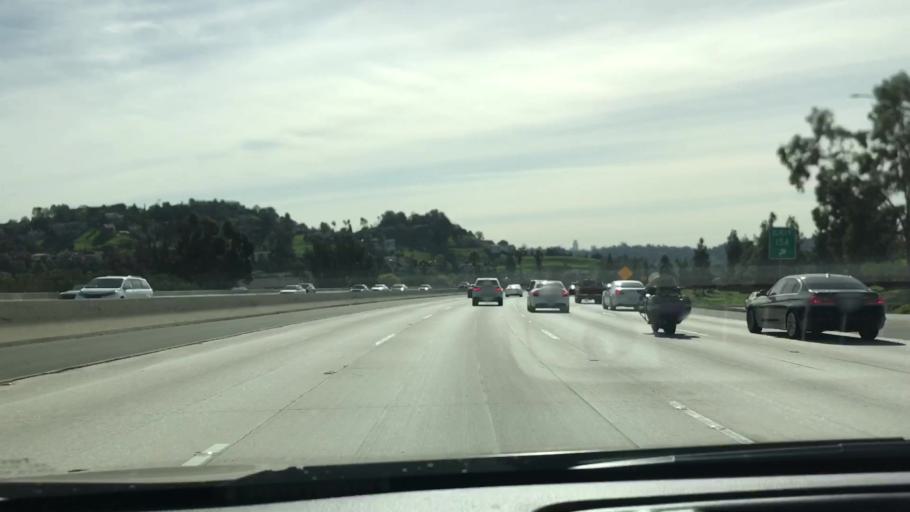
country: US
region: California
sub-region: Los Angeles County
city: Glendale
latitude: 34.1249
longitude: -118.2298
